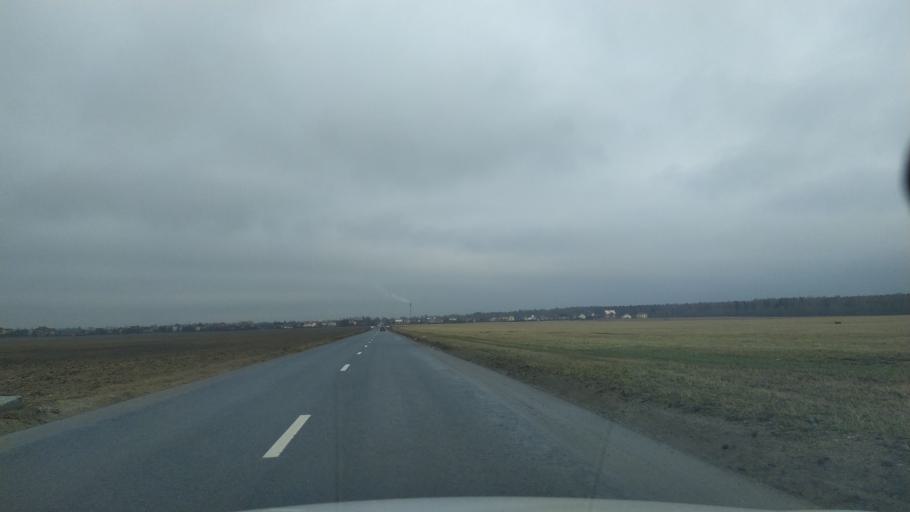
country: RU
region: St.-Petersburg
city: Aleksandrovskaya
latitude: 59.7149
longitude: 30.3351
